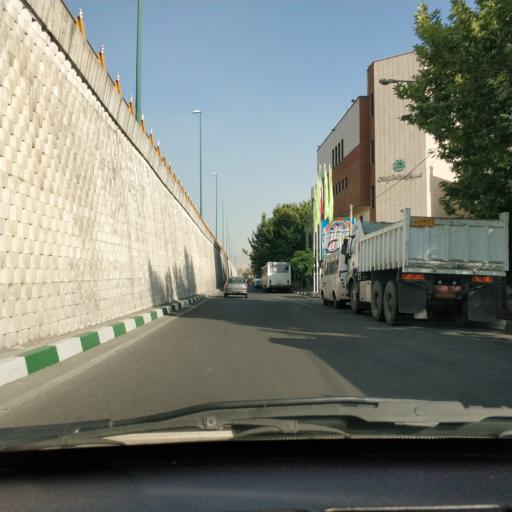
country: IR
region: Tehran
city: Tehran
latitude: 35.7234
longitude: 51.4726
